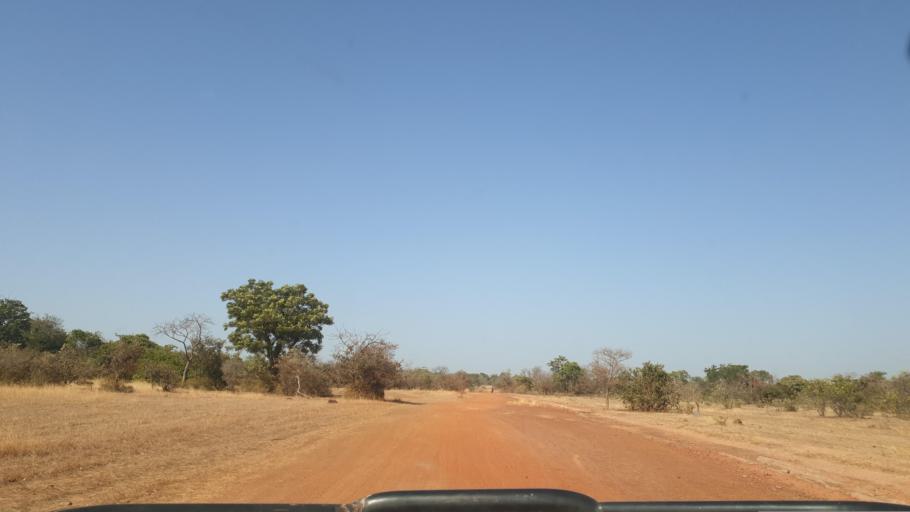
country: ML
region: Sikasso
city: Bougouni
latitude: 11.8185
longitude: -6.9442
